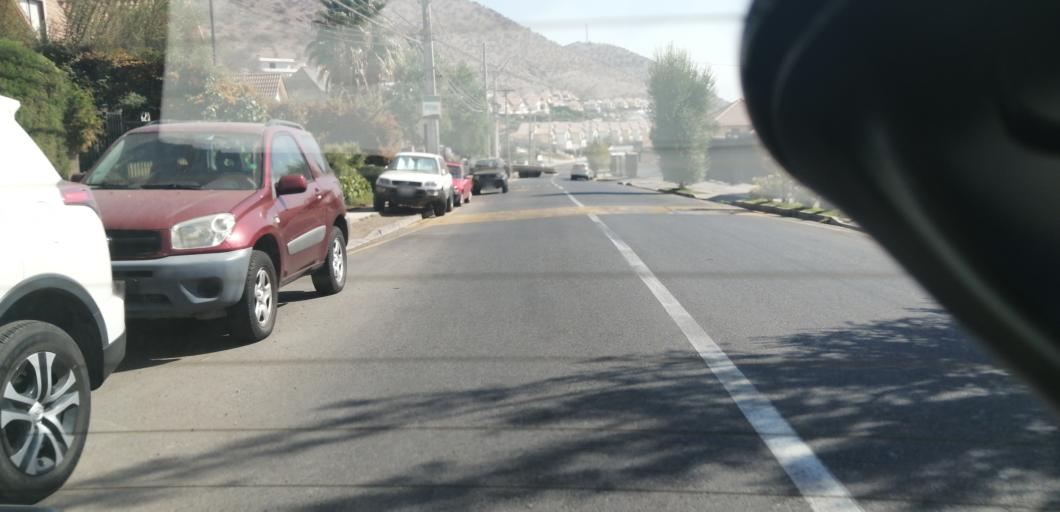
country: CL
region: Santiago Metropolitan
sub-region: Provincia de Santiago
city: Lo Prado
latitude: -33.4525
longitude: -70.8231
